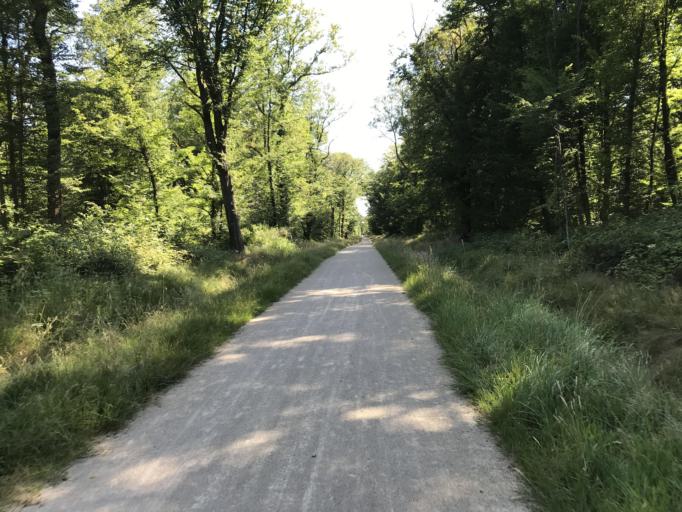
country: FR
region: Ile-de-France
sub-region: Departement de l'Essonne
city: Grigny
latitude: 48.6349
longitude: 2.3861
